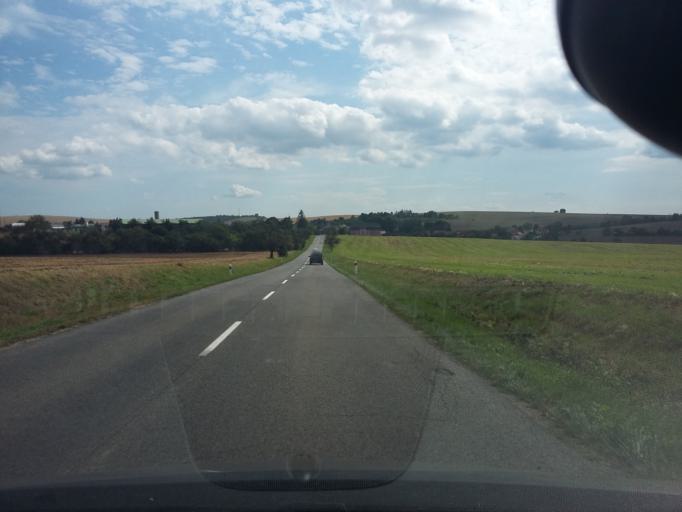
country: SK
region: Trnavsky
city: Gbely
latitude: 48.7306
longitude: 17.1639
